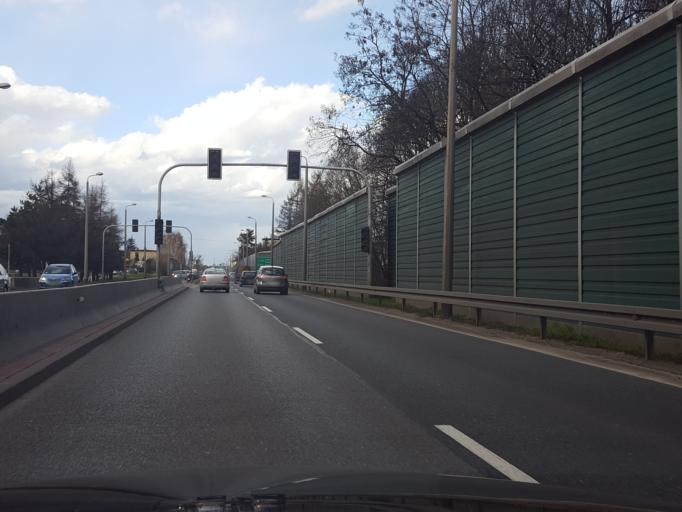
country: PL
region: Silesian Voivodeship
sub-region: Powiat pszczynski
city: Pszczyna
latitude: 49.9696
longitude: 18.9582
